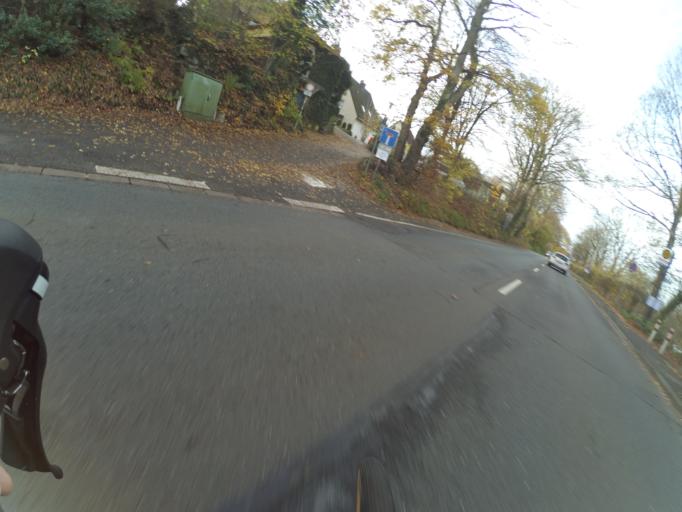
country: DE
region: North Rhine-Westphalia
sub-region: Regierungsbezirk Munster
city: Tecklenburg
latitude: 52.2206
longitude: 7.8009
